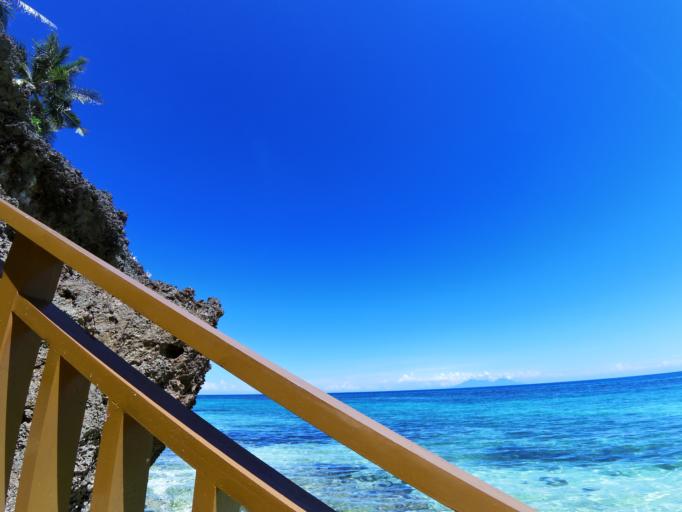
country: PH
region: Central Visayas
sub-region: Province of Bohol
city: Candabong
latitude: 9.7267
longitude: 124.5325
